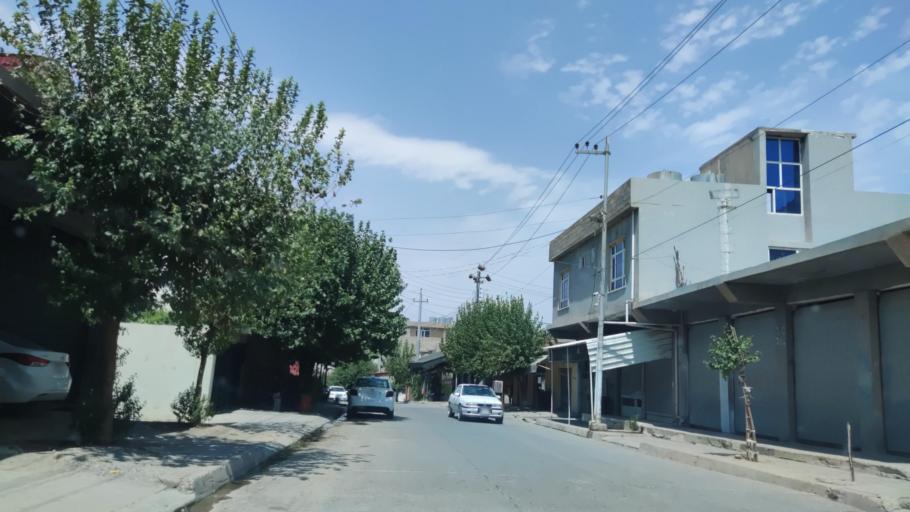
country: IQ
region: Arbil
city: Shaqlawah
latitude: 36.5510
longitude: 44.3561
